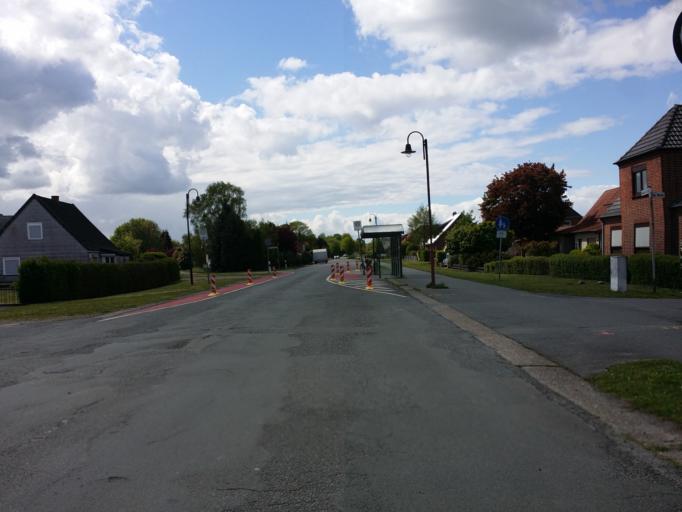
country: DE
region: Lower Saxony
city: Stuhr
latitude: 53.0001
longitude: 8.7731
